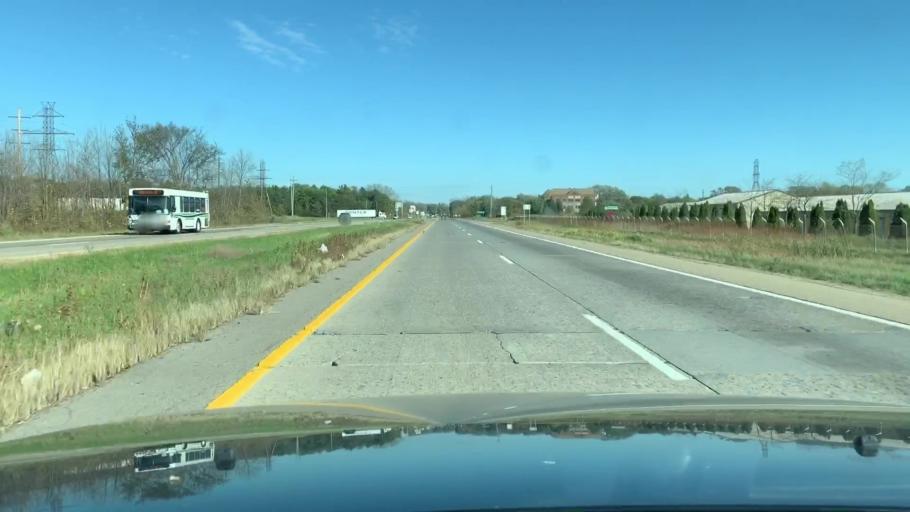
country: US
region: Michigan
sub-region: Ottawa County
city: Zeeland
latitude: 42.8040
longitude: -86.0535
